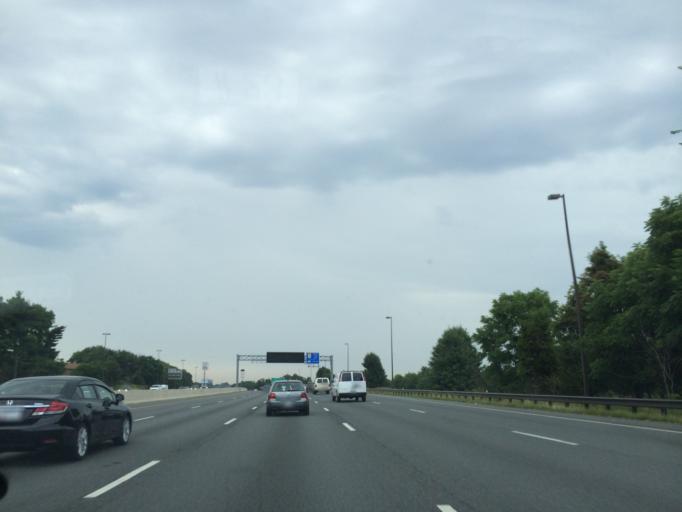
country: US
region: Maryland
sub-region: Montgomery County
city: Gaithersburg
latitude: 39.1365
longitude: -77.2107
